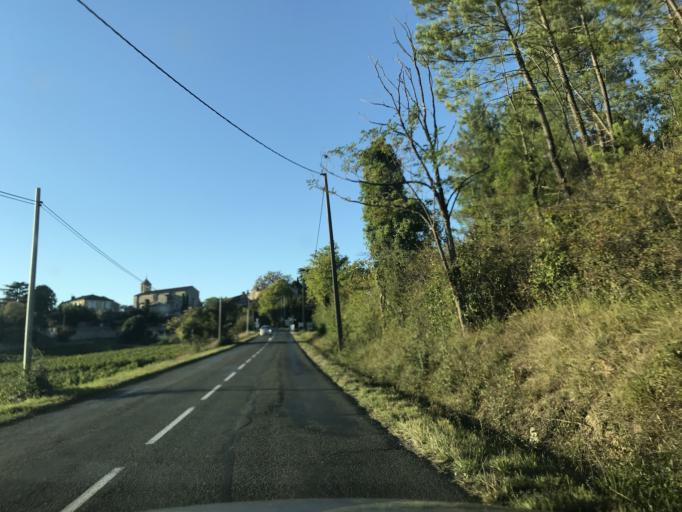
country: FR
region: Aquitaine
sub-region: Departement de la Gironde
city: Lussac
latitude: 44.9212
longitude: -0.0714
